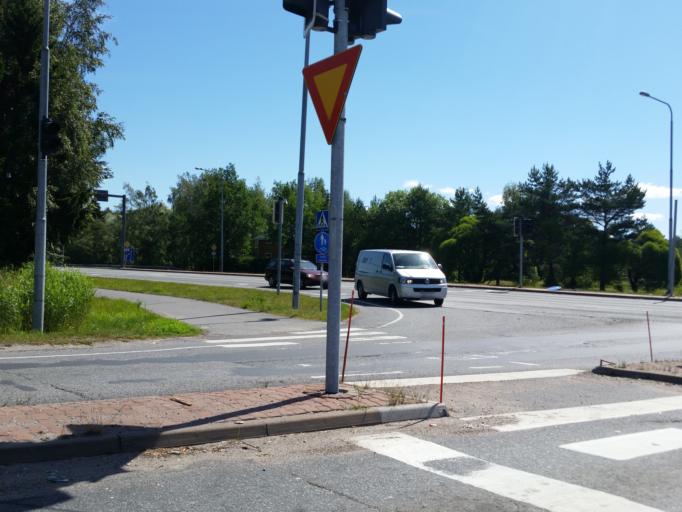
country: FI
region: Varsinais-Suomi
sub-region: Turku
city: Kaarina
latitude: 60.4097
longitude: 22.3842
